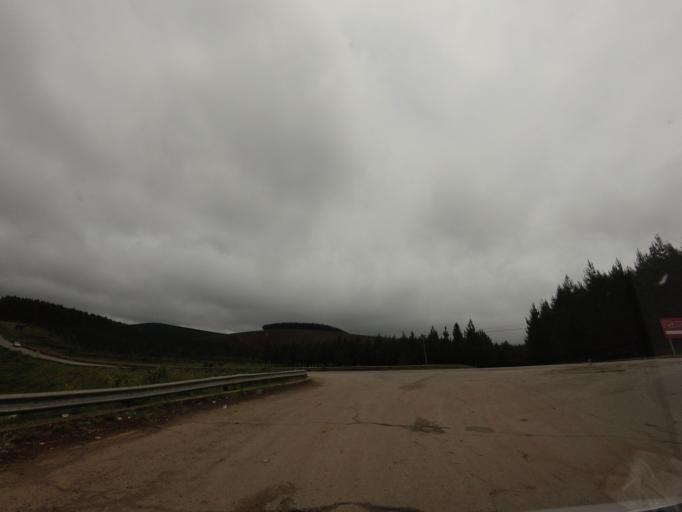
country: SZ
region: Hhohho
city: Piggs Peak
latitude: -25.9856
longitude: 31.2394
